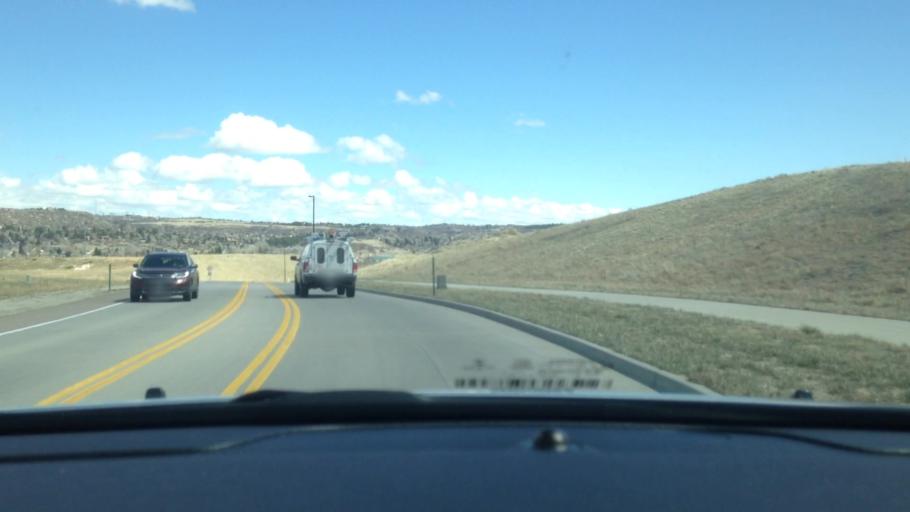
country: US
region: Colorado
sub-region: Douglas County
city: Castle Rock
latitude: 39.3693
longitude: -104.8757
